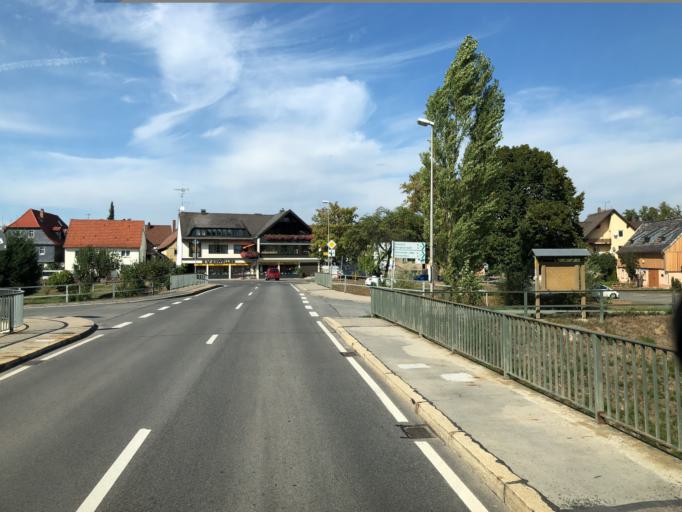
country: DE
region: Bavaria
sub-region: Upper Franconia
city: Michelau
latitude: 50.1606
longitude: 11.1144
